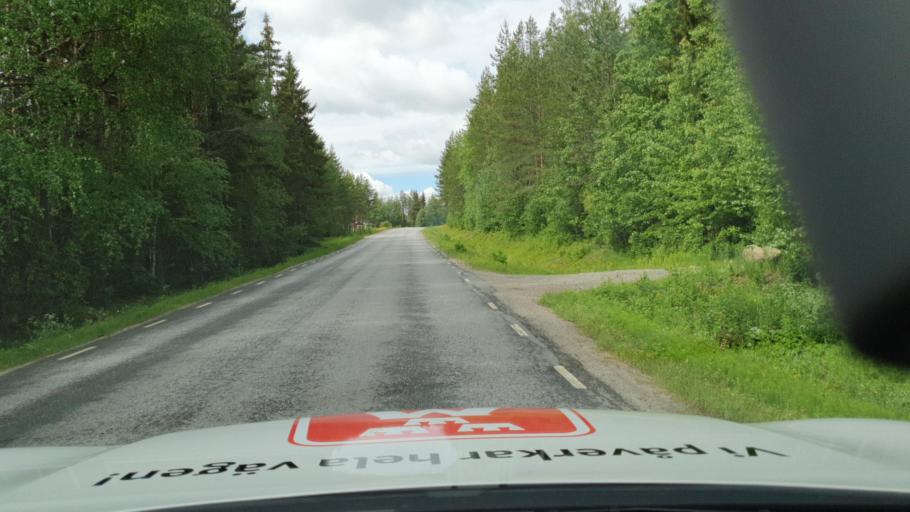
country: SE
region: Vaesterbotten
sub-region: Dorotea Kommun
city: Dorotea
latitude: 64.2642
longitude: 16.3600
